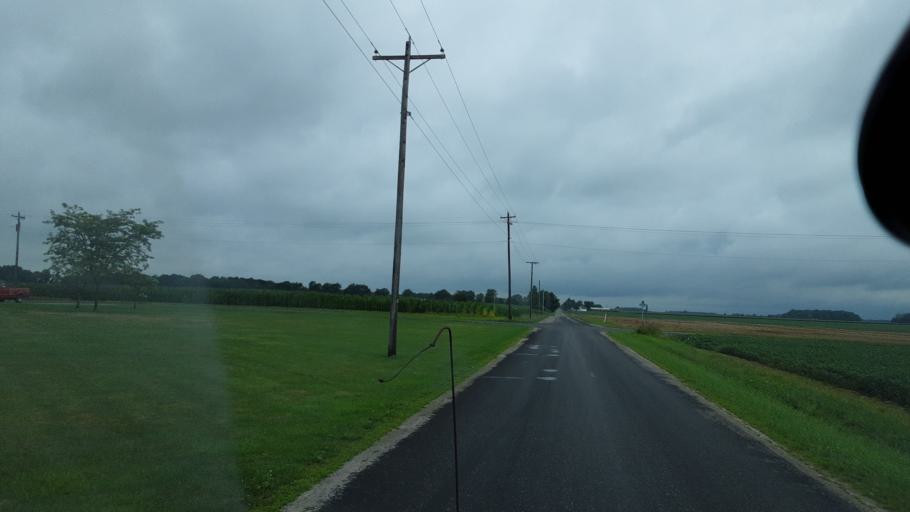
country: US
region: Indiana
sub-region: Allen County
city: Monroeville
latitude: 40.8908
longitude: -84.8424
